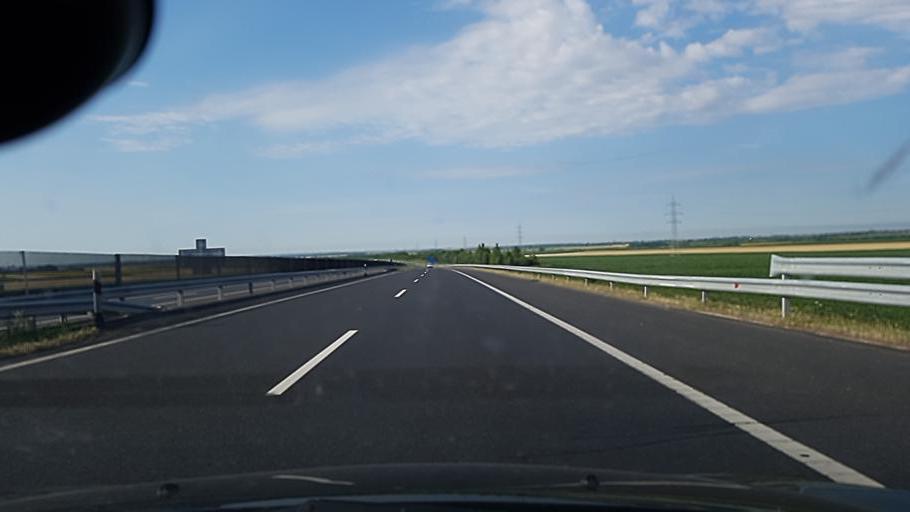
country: HU
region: Fejer
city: Ivancsa
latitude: 47.1681
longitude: 18.8036
